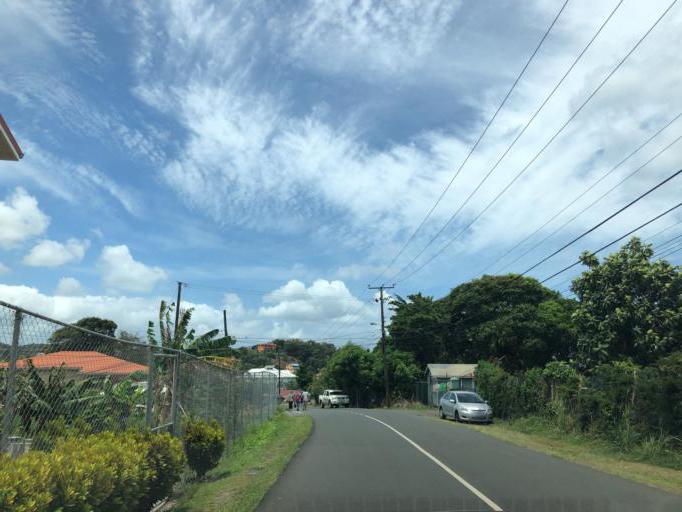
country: LC
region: Castries Quarter
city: Castries
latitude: 13.9940
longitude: -61.0064
